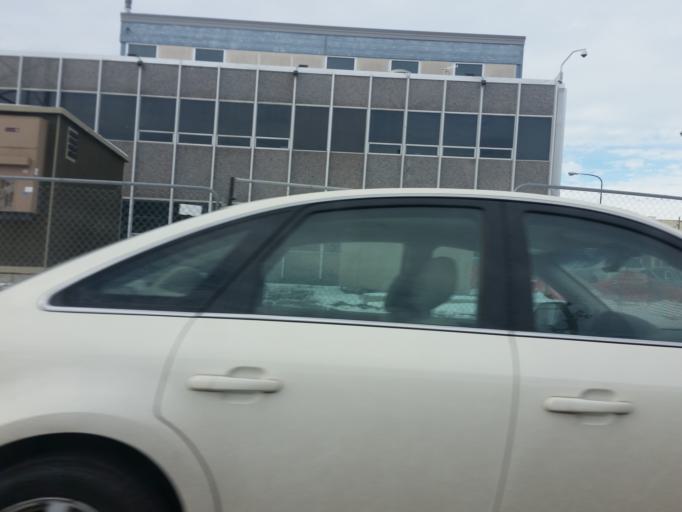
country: US
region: Iowa
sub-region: Black Hawk County
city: Waterloo
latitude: 42.4987
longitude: -92.3317
